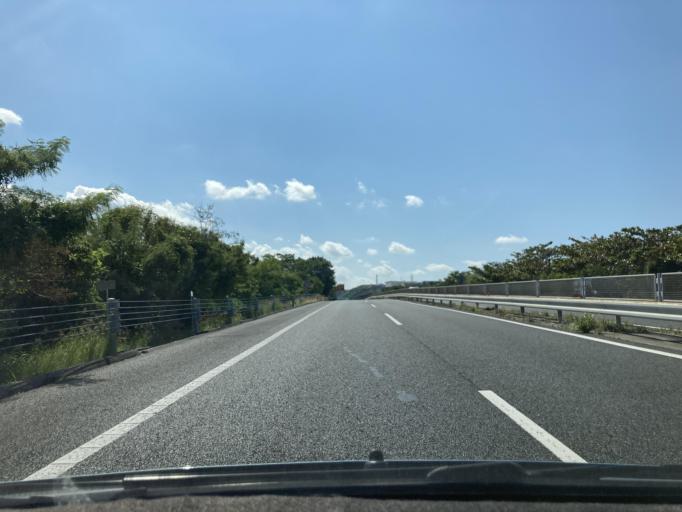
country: JP
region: Okinawa
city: Ginowan
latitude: 26.2318
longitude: 127.7394
